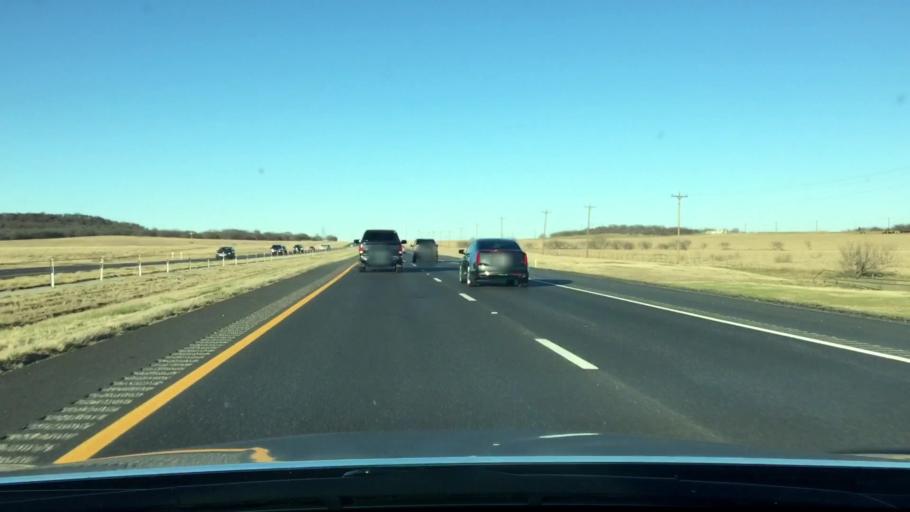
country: US
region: Texas
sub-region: Denton County
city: Argyle
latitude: 33.1374
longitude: -97.2014
